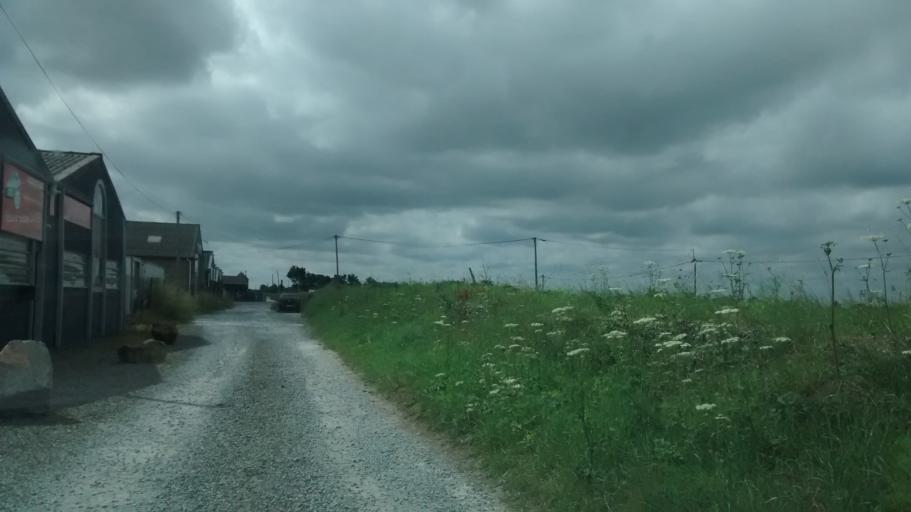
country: FR
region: Brittany
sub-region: Departement d'Ille-et-Vilaine
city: Saint-Meloir-des-Ondes
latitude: 48.6377
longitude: -1.8680
